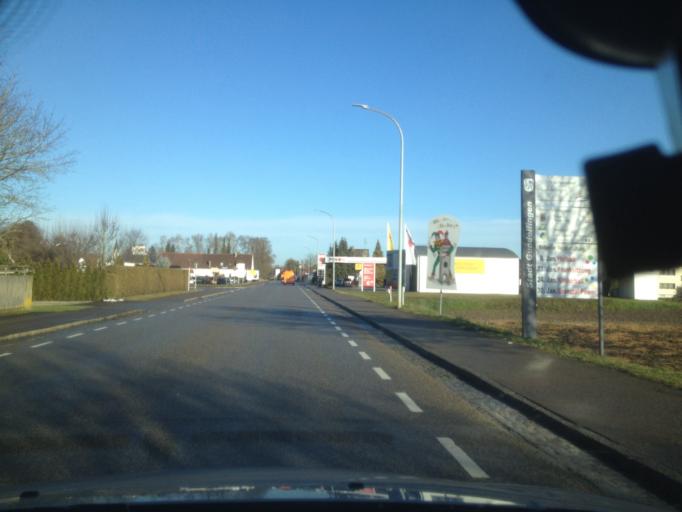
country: DE
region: Bavaria
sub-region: Swabia
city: Gundelfingen
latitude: 48.5429
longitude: 10.3671
